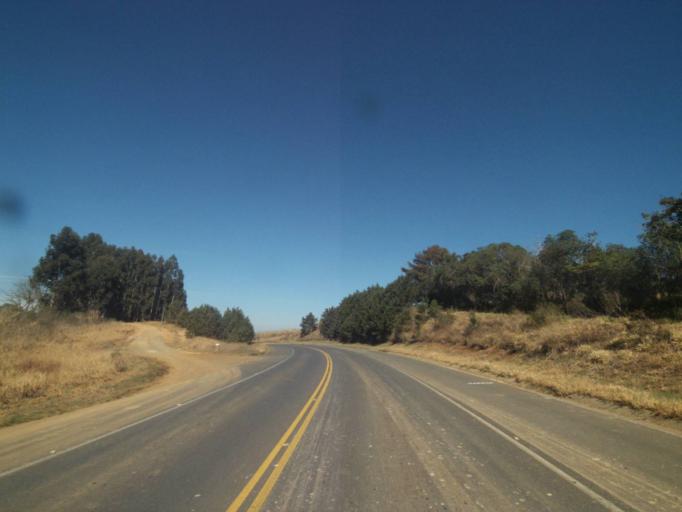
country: BR
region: Parana
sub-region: Tibagi
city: Tibagi
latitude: -24.5282
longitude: -50.4476
